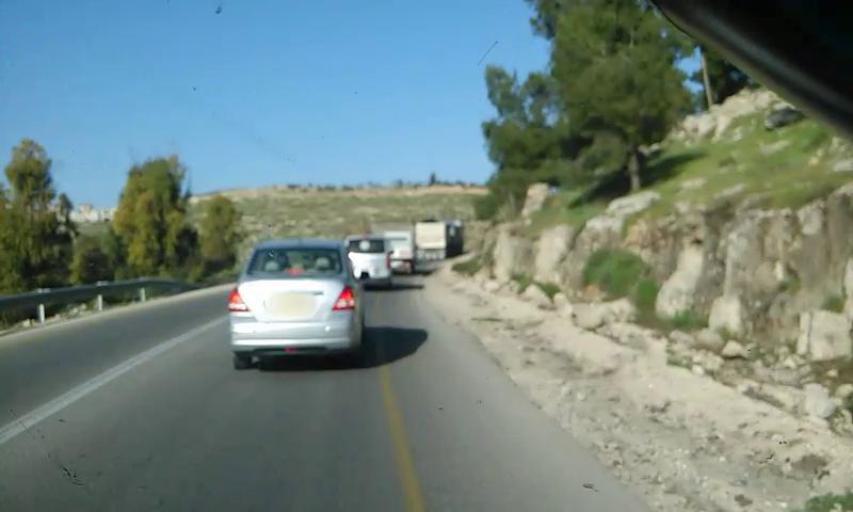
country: PS
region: West Bank
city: Ar Rihiyah
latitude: 31.4911
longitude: 35.0682
